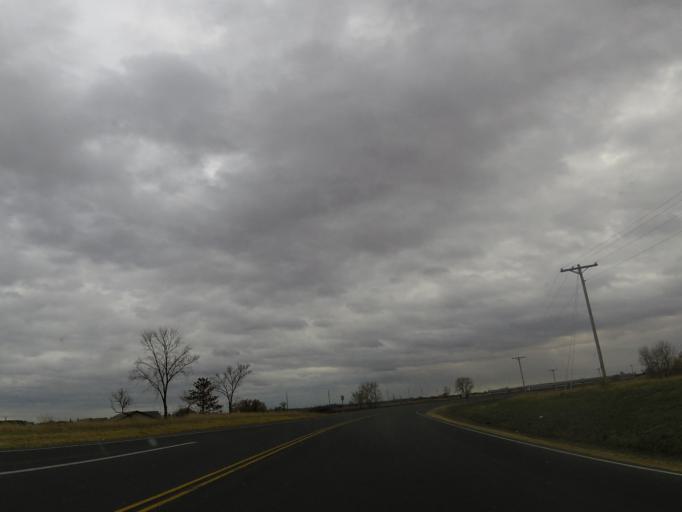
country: US
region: Wisconsin
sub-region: Saint Croix County
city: New Richmond
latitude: 45.1005
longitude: -92.5585
